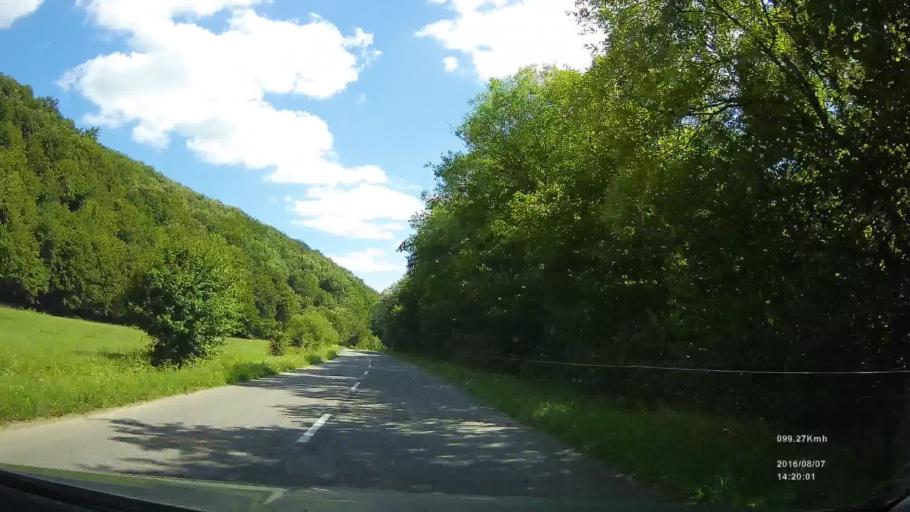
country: SK
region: Presovsky
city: Stropkov
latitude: 49.2955
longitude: 21.7580
